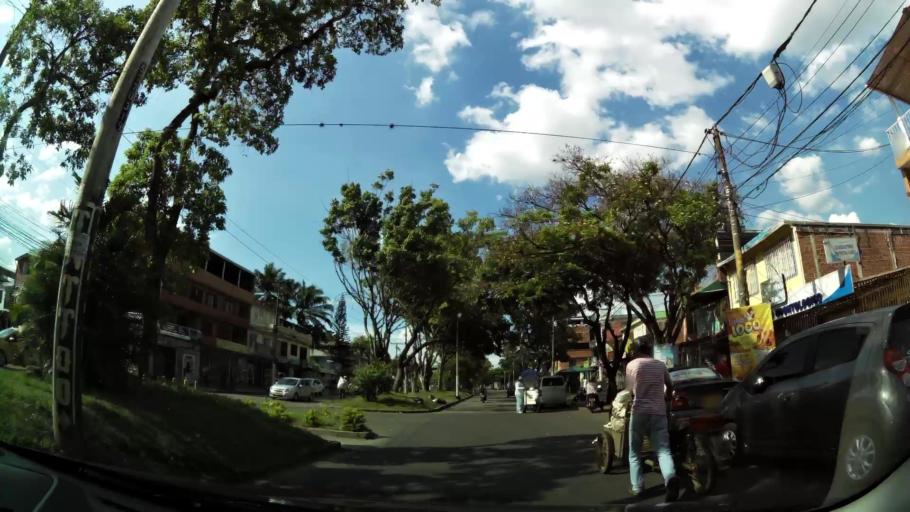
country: CO
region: Valle del Cauca
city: Cali
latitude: 3.4114
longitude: -76.5181
